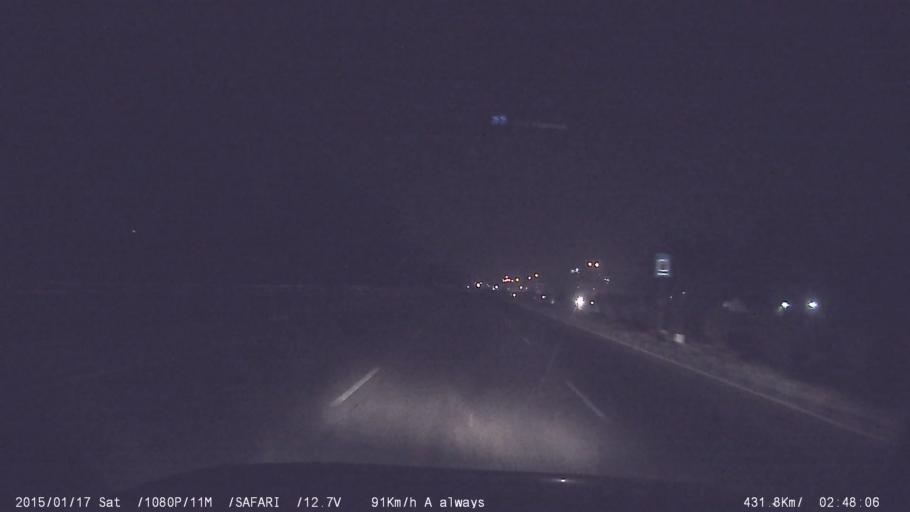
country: IN
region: Karnataka
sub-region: Bangalore Urban
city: Anekal
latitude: 12.8156
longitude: 77.6921
